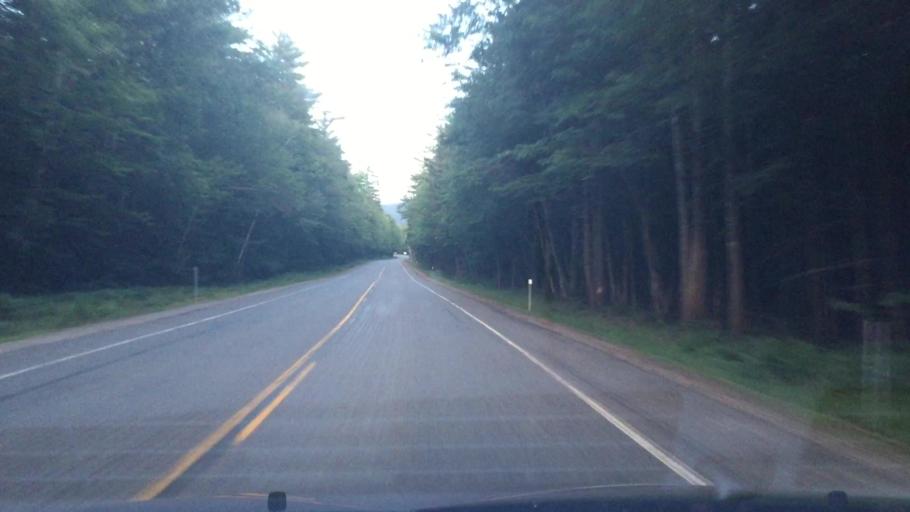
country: US
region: New Hampshire
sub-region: Grafton County
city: Woodstock
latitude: 44.0422
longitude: -71.5506
